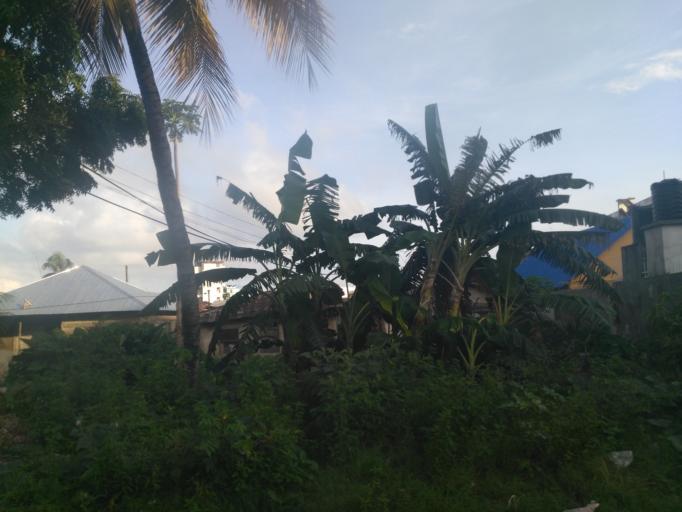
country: TZ
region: Zanzibar Urban/West
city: Zanzibar
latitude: -6.1694
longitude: 39.1980
